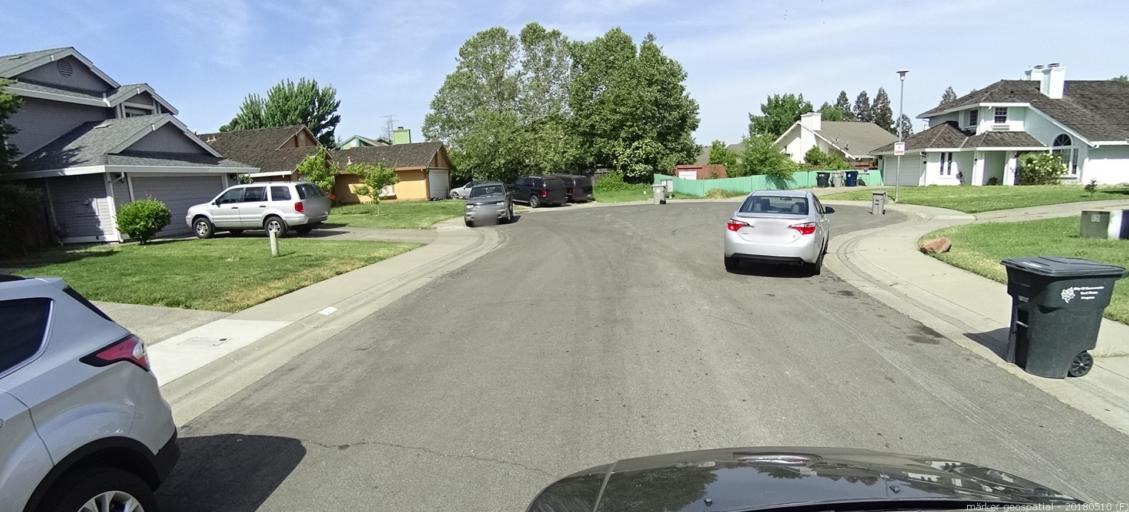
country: US
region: California
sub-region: Sacramento County
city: Rio Linda
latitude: 38.6588
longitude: -121.4627
